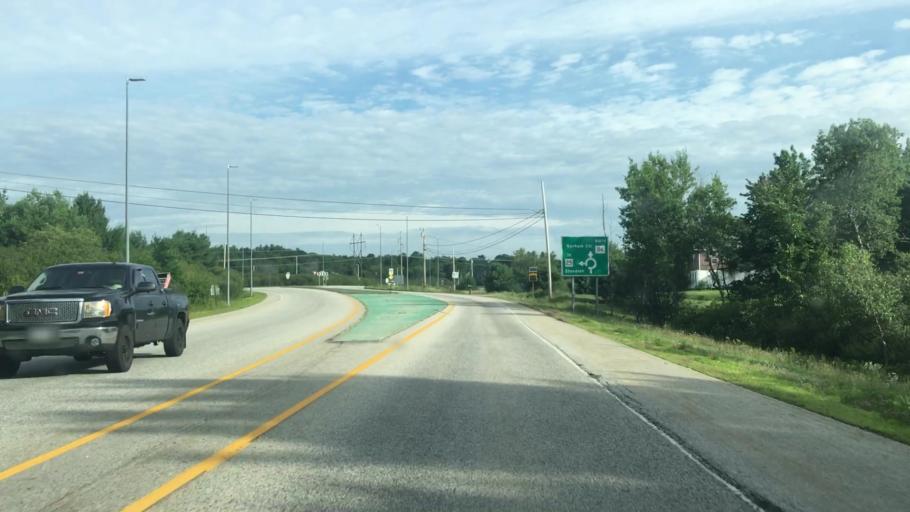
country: US
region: Maine
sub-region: Cumberland County
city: Gorham
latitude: 43.6506
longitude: -70.4260
